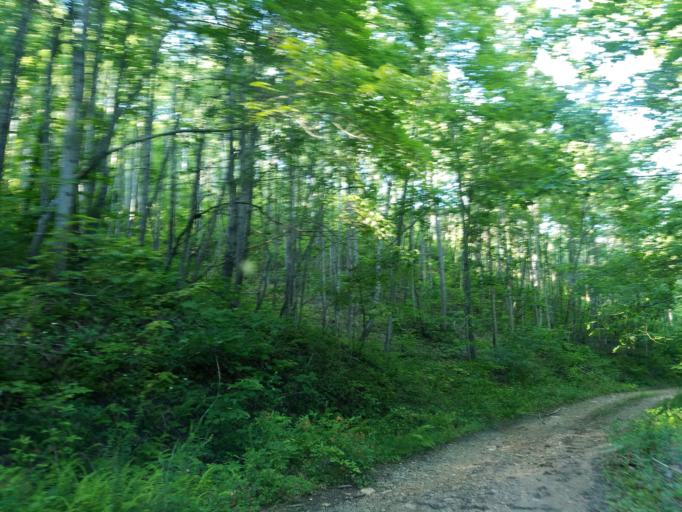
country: US
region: Georgia
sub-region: Fannin County
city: Blue Ridge
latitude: 34.8041
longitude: -84.1771
